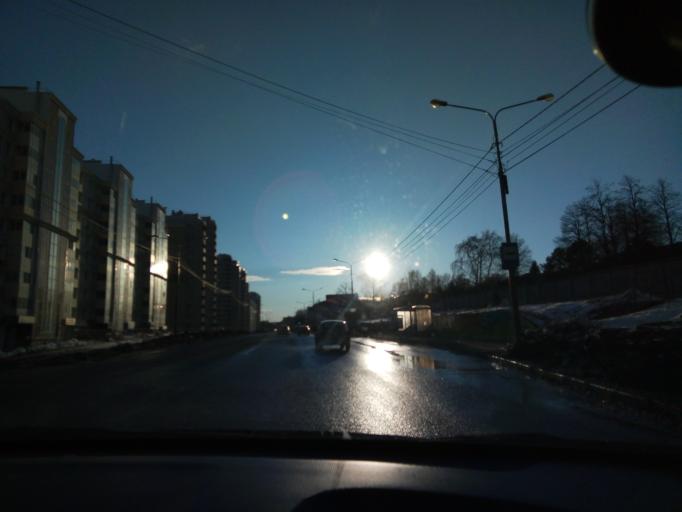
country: RU
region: Chuvashia
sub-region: Cheboksarskiy Rayon
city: Cheboksary
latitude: 56.1410
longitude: 47.2230
